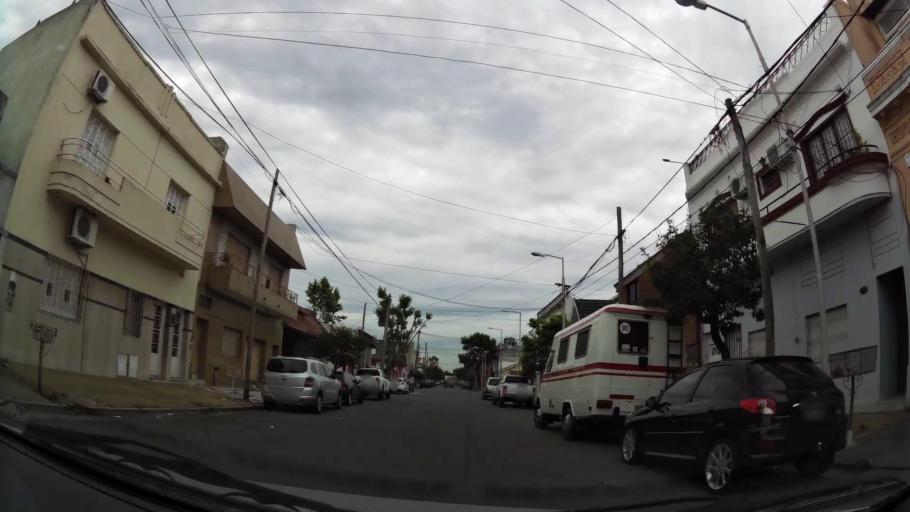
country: AR
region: Buenos Aires
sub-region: Partido de Avellaneda
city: Avellaneda
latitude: -34.6734
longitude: -58.3913
